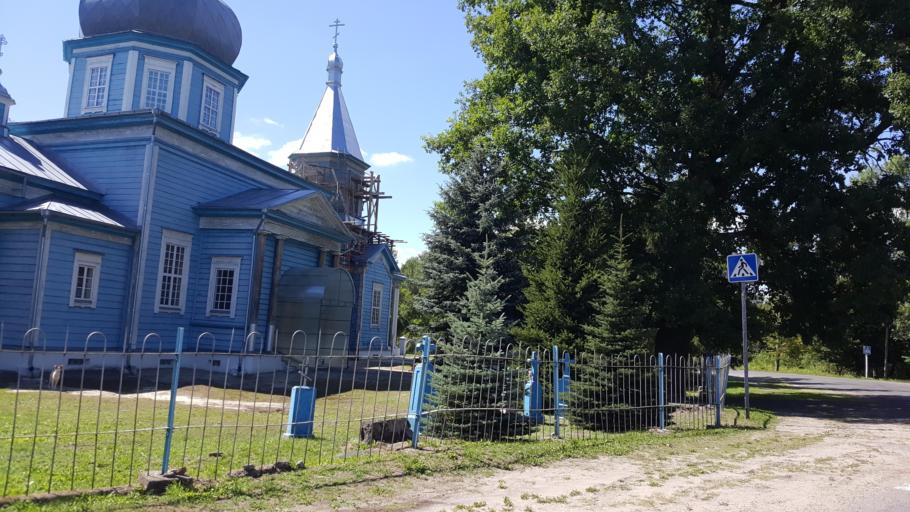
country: BY
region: Brest
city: Horad Kobryn
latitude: 52.3002
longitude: 24.3687
